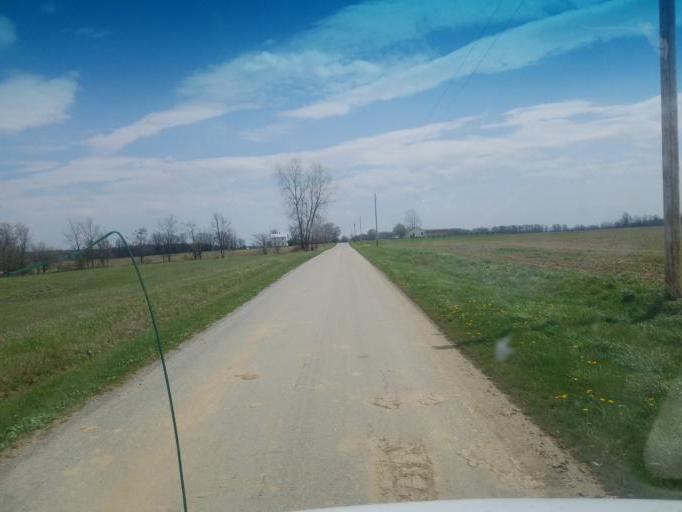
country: US
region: Ohio
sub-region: Hardin County
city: Forest
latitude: 40.7742
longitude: -83.4450
